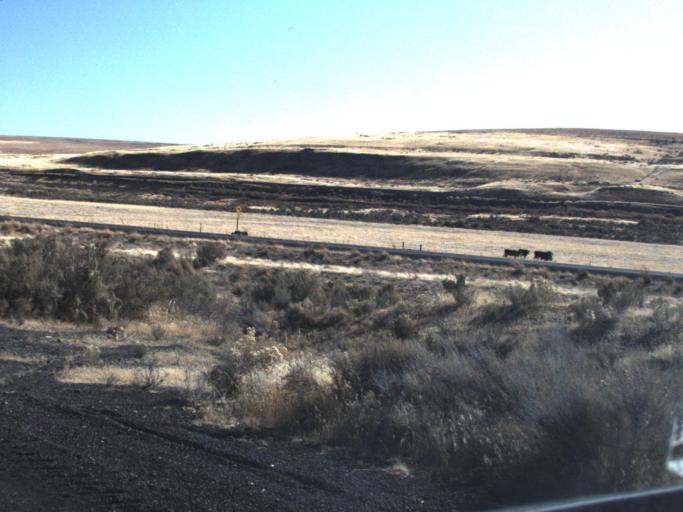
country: US
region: Washington
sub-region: Adams County
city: Ritzville
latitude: 46.9707
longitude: -118.6627
